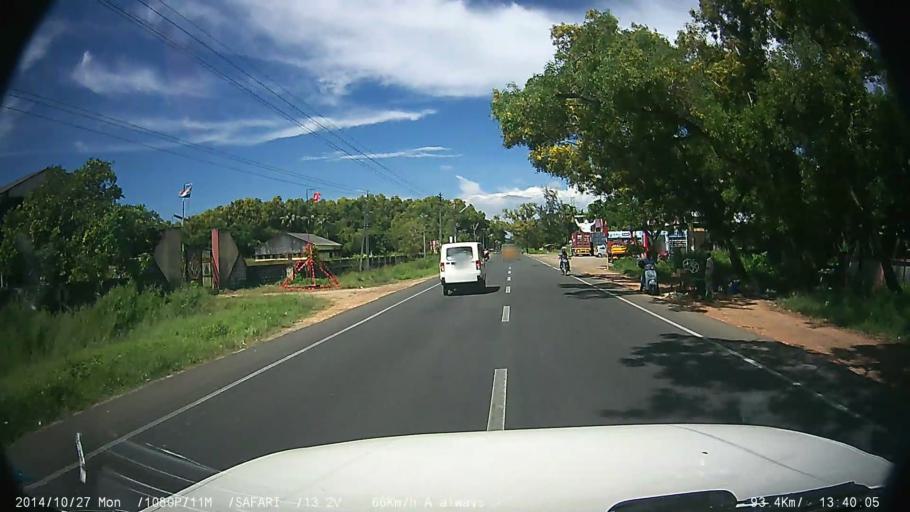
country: IN
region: Kerala
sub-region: Alappuzha
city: Shertallai
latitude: 9.6315
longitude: 76.3336
